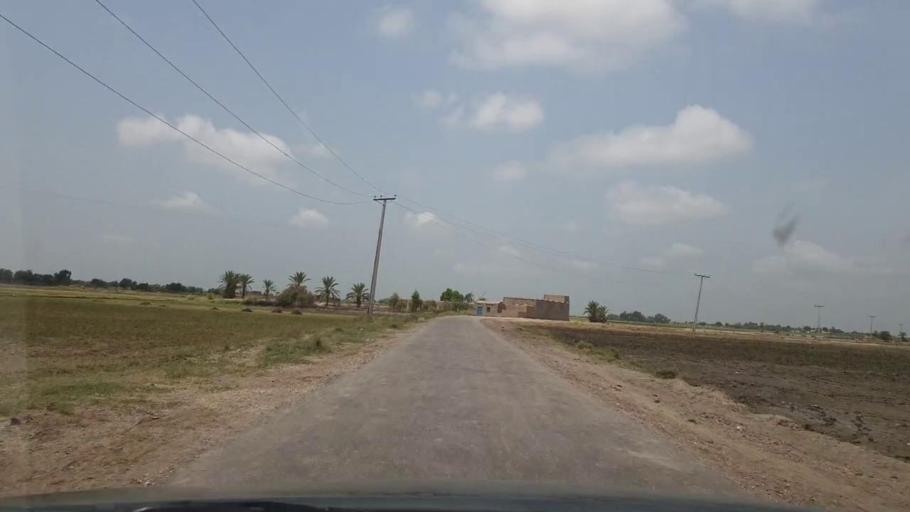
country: PK
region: Sindh
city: Ratodero
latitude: 27.9035
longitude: 68.3178
